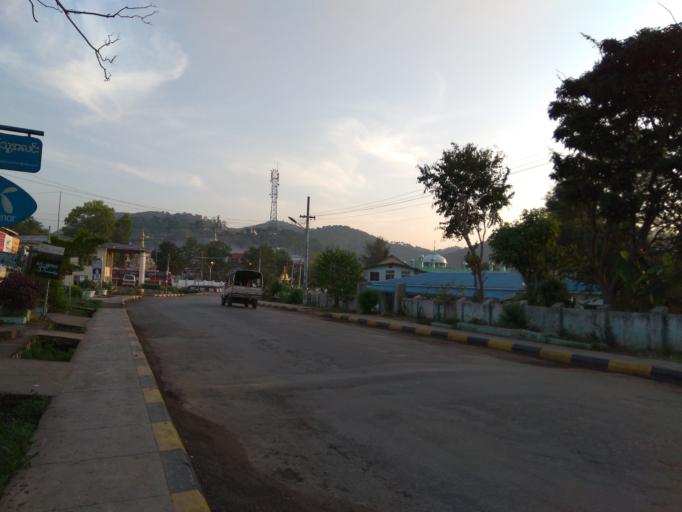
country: MM
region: Mandalay
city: Yamethin
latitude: 20.6324
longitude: 96.5660
